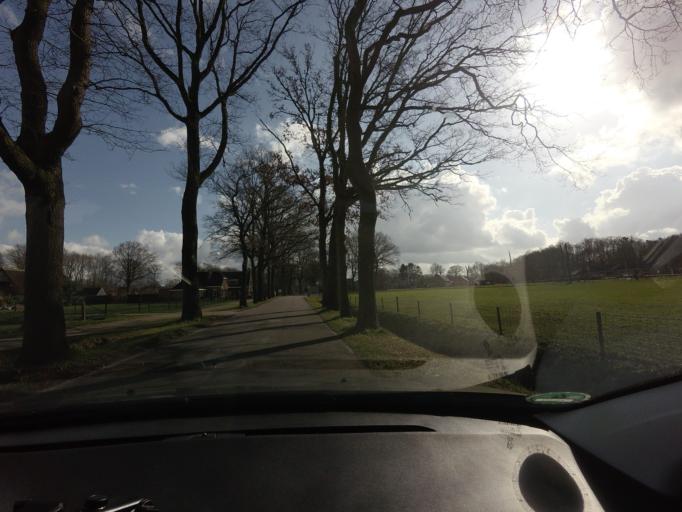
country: NL
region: Drenthe
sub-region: Gemeente Assen
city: Assen
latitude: 52.8544
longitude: 6.5982
